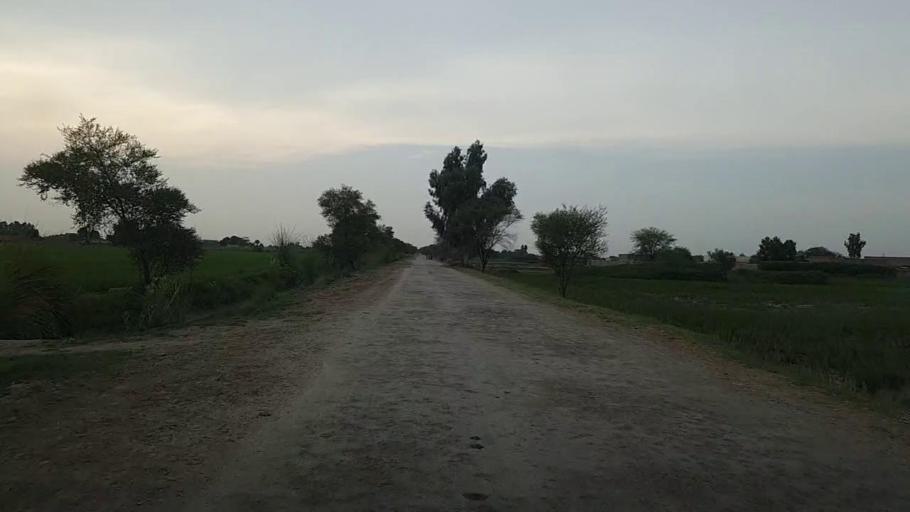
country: PK
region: Sindh
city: Khanpur
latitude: 27.8439
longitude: 69.4623
